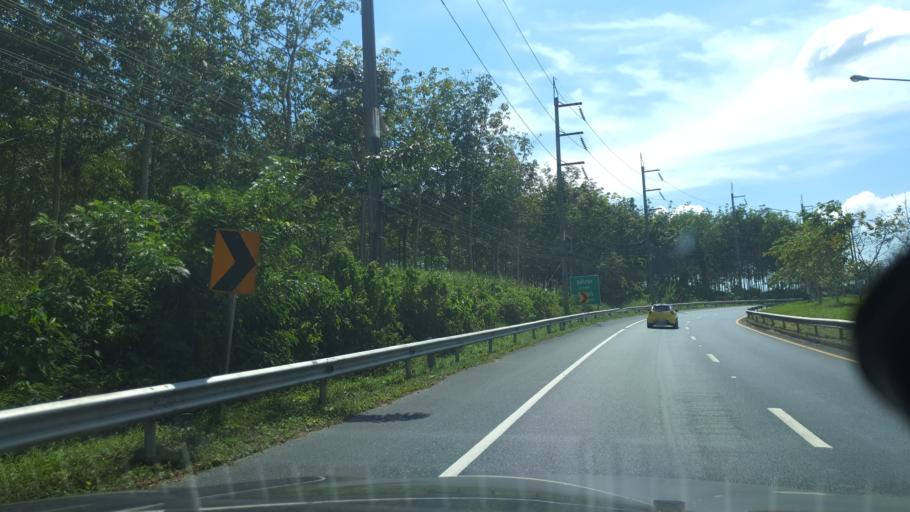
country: TH
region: Phangnga
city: Takua Thung
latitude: 8.2913
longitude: 98.3746
